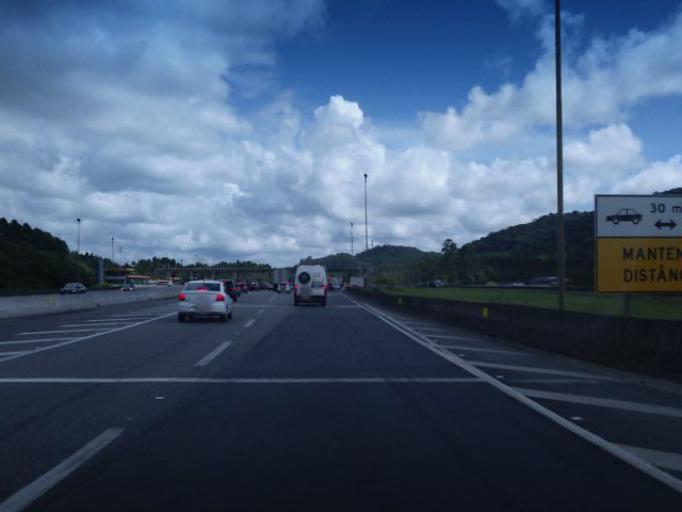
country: BR
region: Santa Catarina
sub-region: Barra Velha
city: Barra Velha
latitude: -26.5944
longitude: -48.7221
